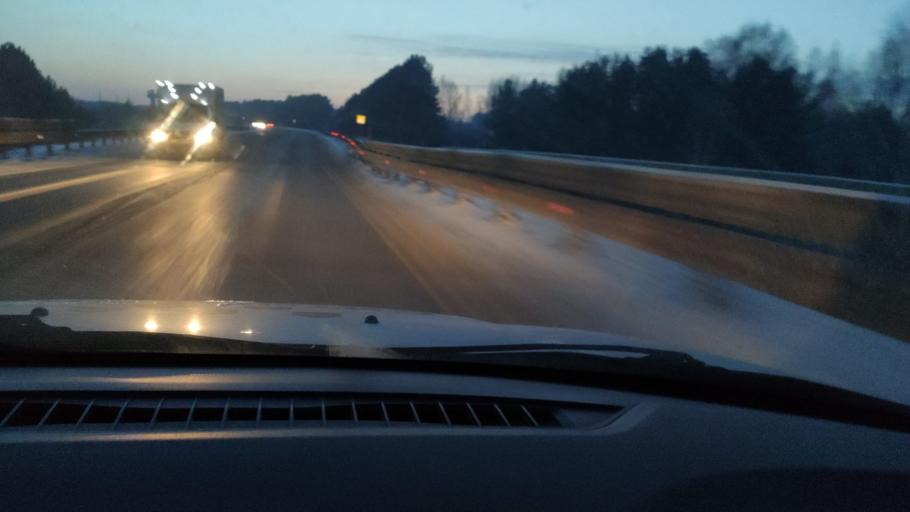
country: RU
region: Perm
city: Kungur
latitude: 57.4217
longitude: 56.9236
